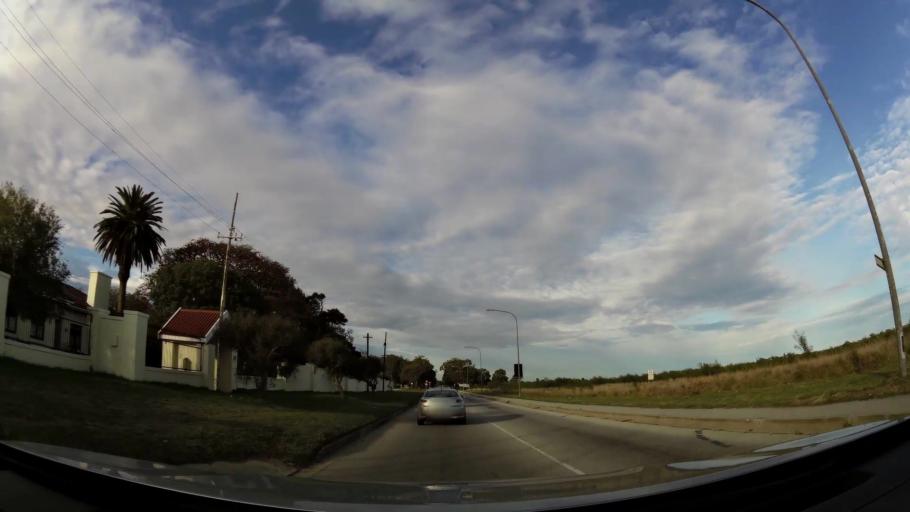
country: ZA
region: Eastern Cape
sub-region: Nelson Mandela Bay Metropolitan Municipality
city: Port Elizabeth
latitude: -33.9585
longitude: 25.4935
